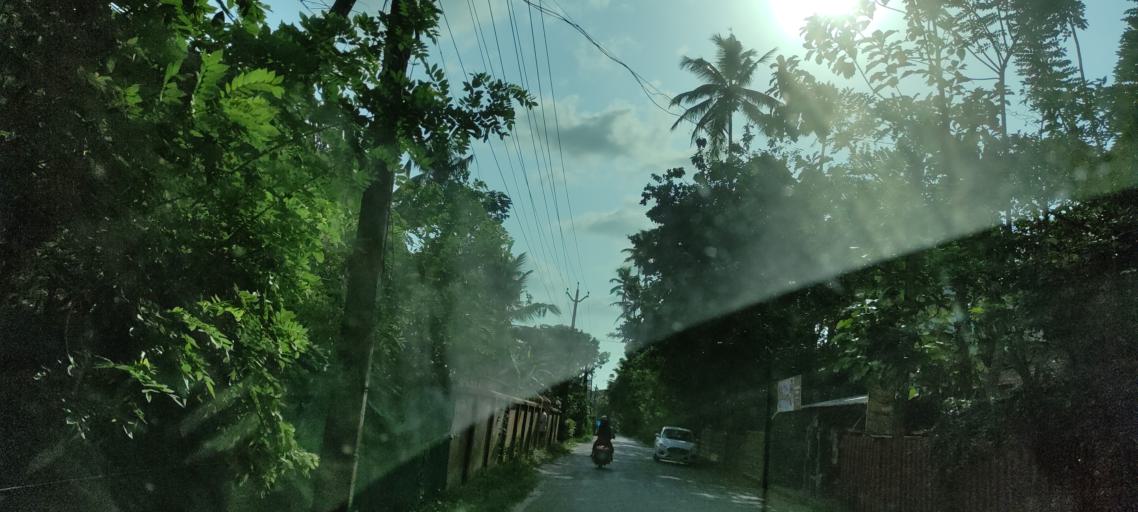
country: IN
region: Kerala
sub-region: Alappuzha
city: Vayalar
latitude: 9.6865
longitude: 76.3074
